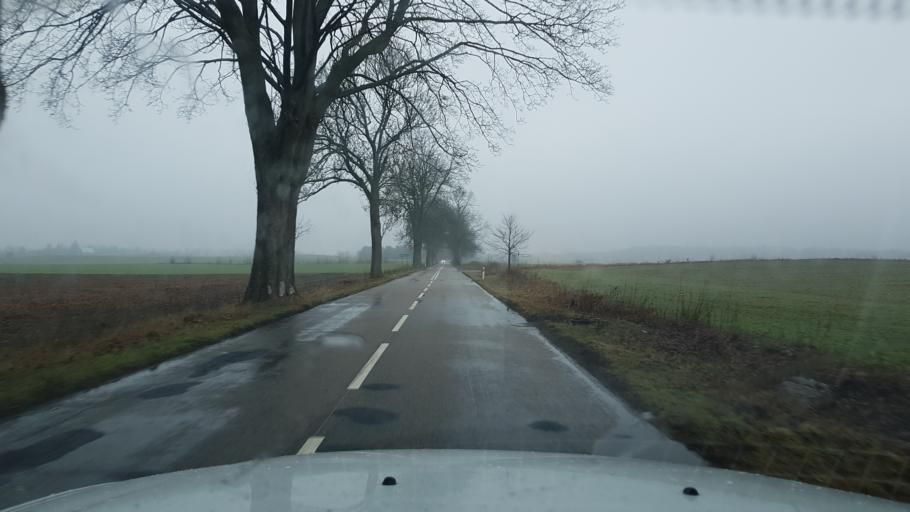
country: PL
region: West Pomeranian Voivodeship
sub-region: Powiat drawski
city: Czaplinek
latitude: 53.5786
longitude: 16.2371
